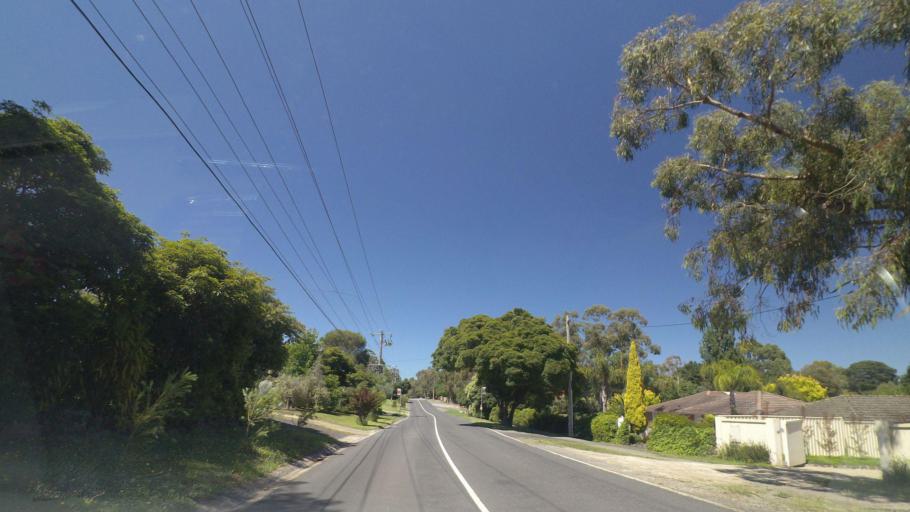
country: AU
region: Victoria
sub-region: Maroondah
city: Warranwood
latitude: -37.7846
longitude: 145.2370
